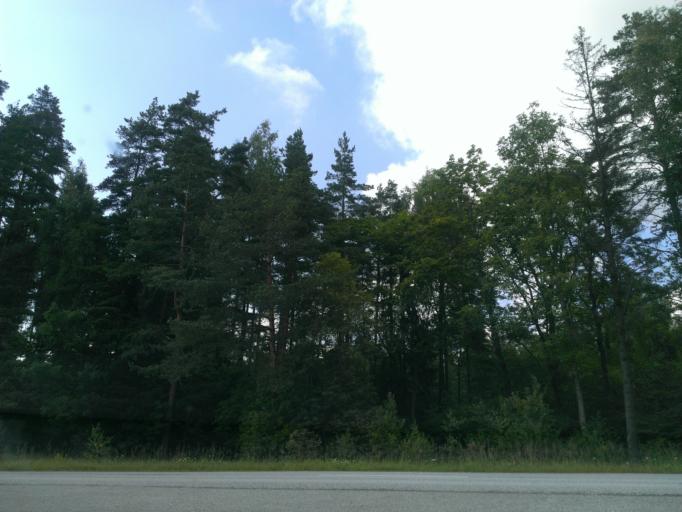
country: LV
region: Priekuli
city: Priekuli
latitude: 57.2934
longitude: 25.4731
